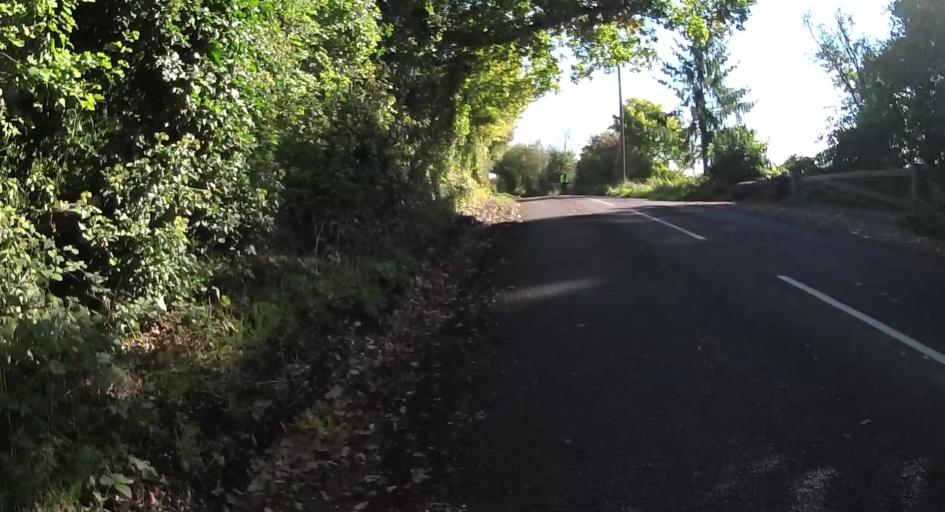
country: GB
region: England
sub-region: Hampshire
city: Old Basing
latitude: 51.2640
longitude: -1.0061
